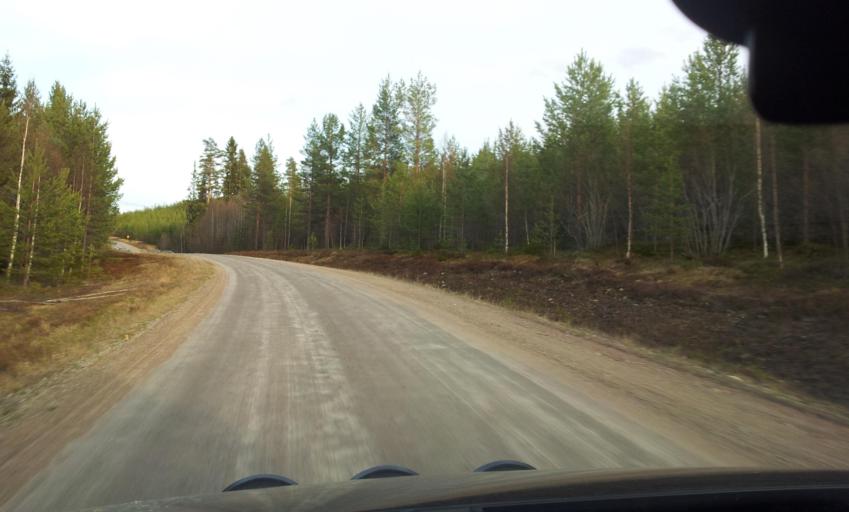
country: SE
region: Gaevleborg
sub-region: Ljusdals Kommun
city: Farila
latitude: 62.1149
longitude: 15.6911
